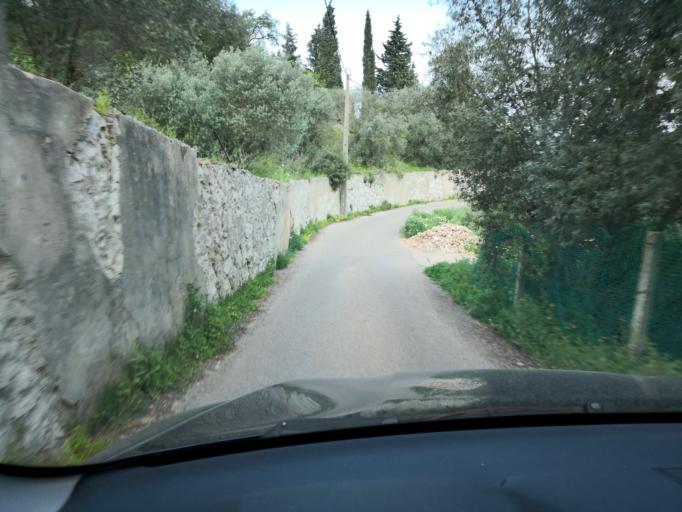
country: PT
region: Setubal
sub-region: Setubal
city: Setubal
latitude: 38.5179
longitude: -8.9151
